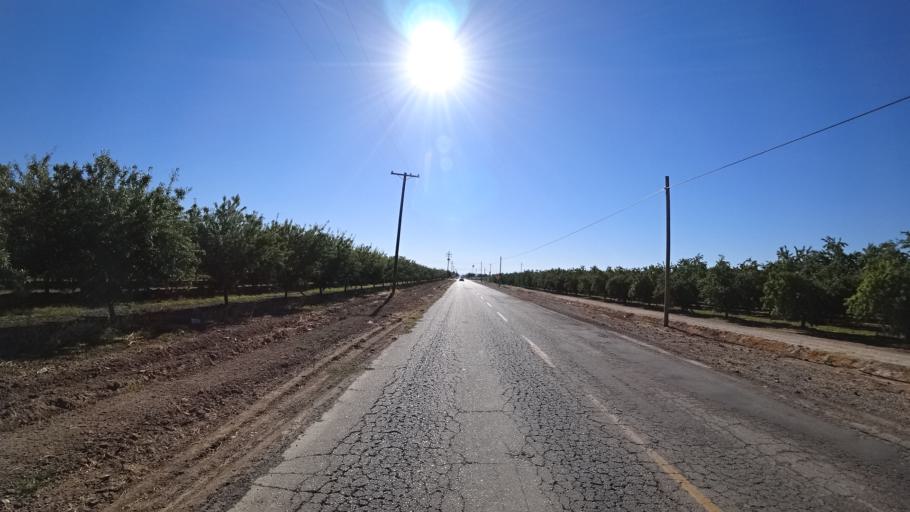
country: US
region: California
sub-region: Fresno County
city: West Park
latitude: 36.6922
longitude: -119.8204
